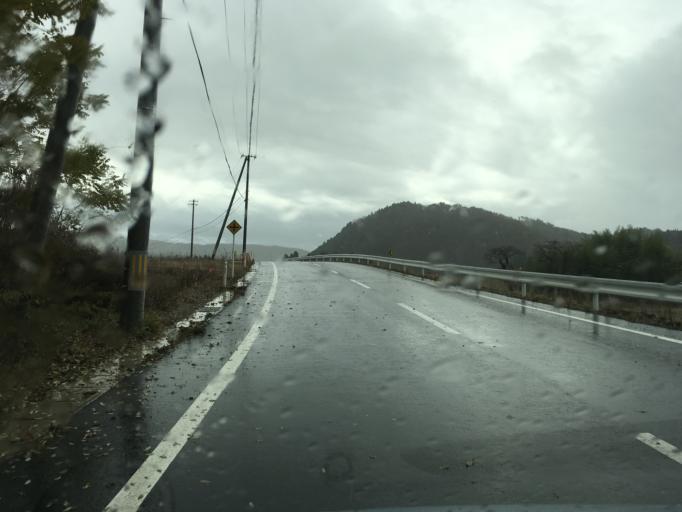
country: JP
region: Iwate
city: Ichinoseki
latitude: 38.7944
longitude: 141.2492
